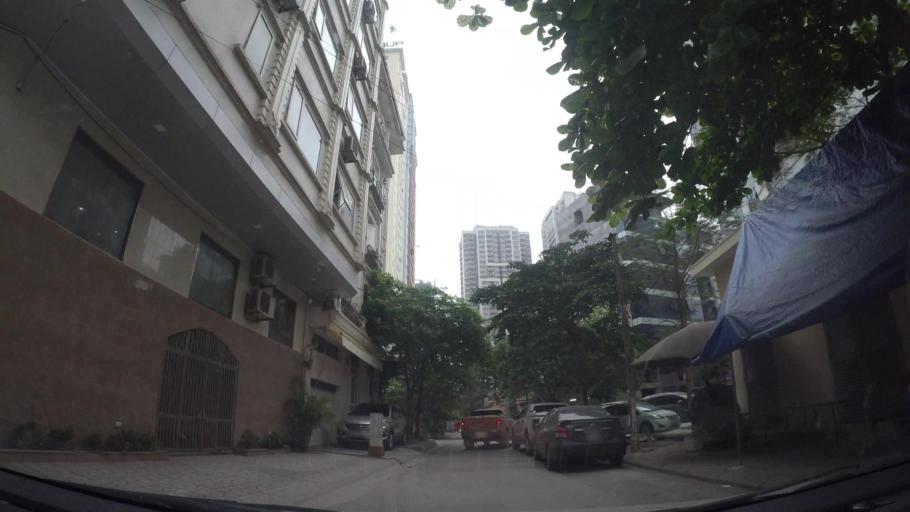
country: VN
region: Ha Noi
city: Cau Dien
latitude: 21.0359
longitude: 105.7720
